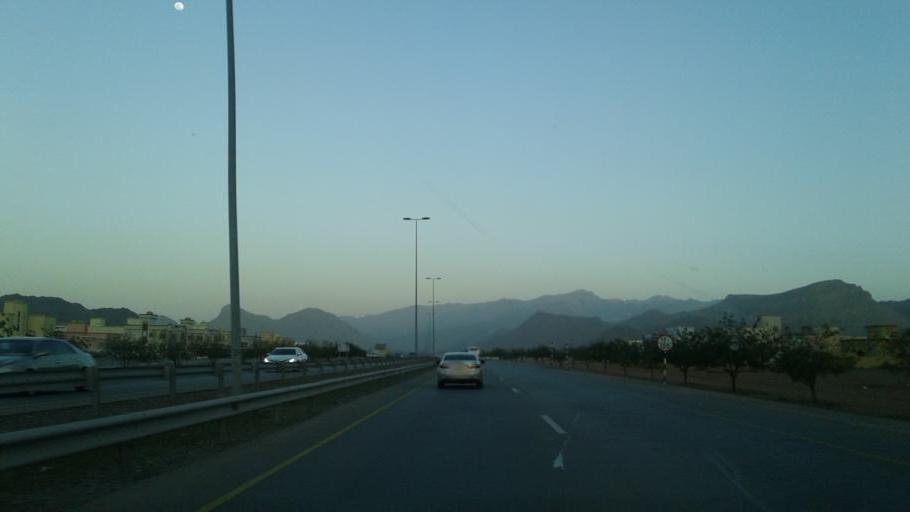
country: OM
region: Muhafazat ad Dakhiliyah
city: Bidbid
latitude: 23.4641
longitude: 58.1527
